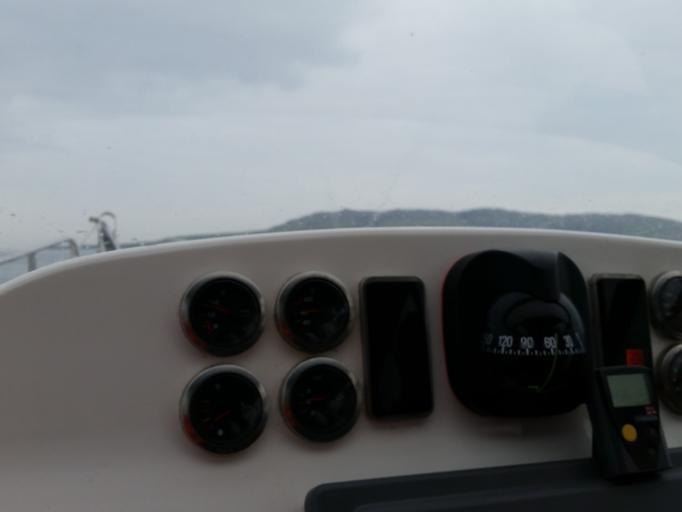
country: IE
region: Leinster
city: Portraine
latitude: 53.4851
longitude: -6.0520
